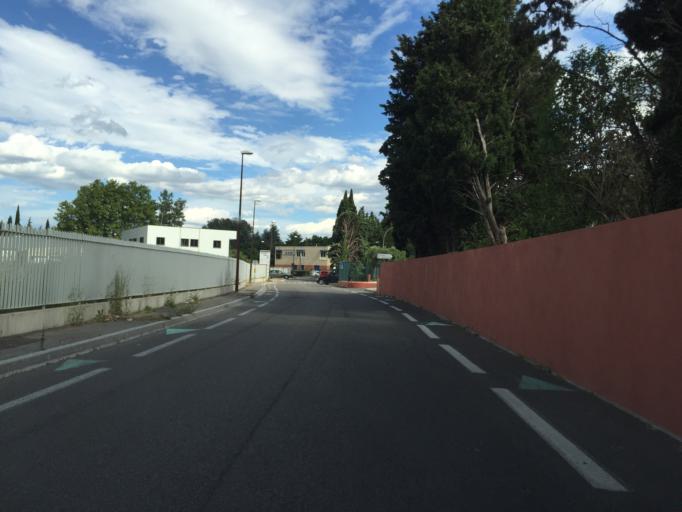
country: FR
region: Provence-Alpes-Cote d'Azur
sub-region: Departement des Bouches-du-Rhone
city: Rognonas
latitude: 43.9235
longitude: 4.8000
